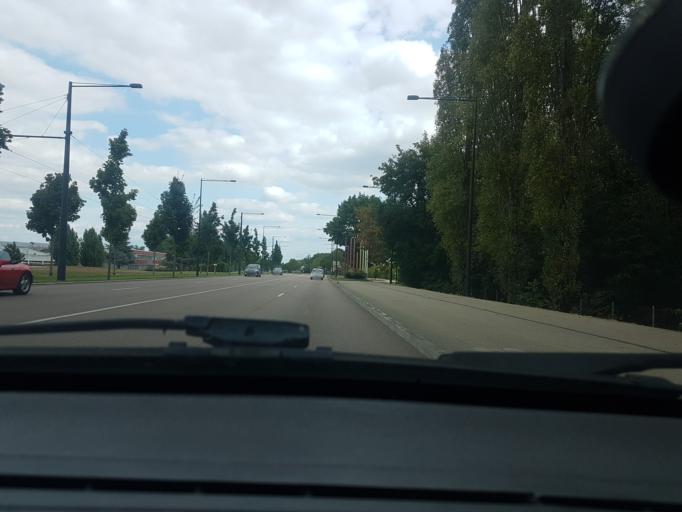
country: FR
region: Bourgogne
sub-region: Departement de la Cote-d'Or
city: Saint-Apollinaire
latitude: 47.3142
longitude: 5.0878
